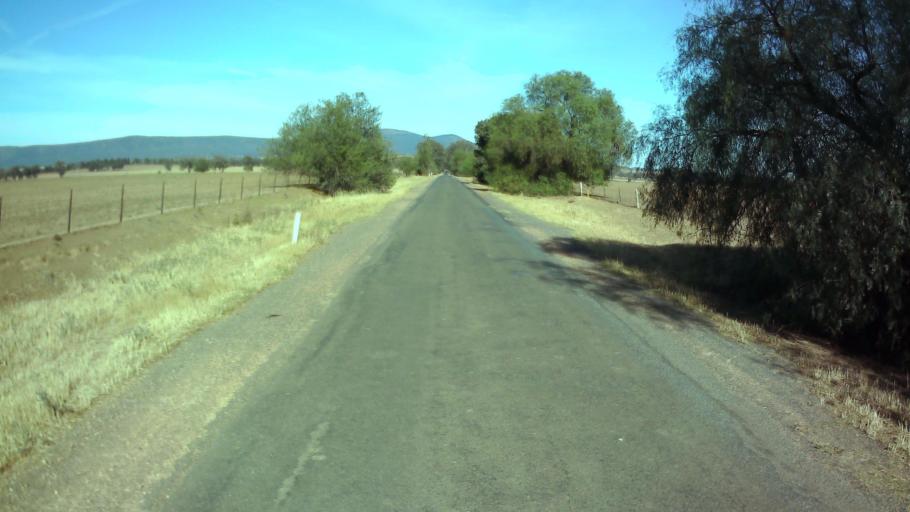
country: AU
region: New South Wales
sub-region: Weddin
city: Grenfell
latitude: -33.9079
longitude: 148.1078
